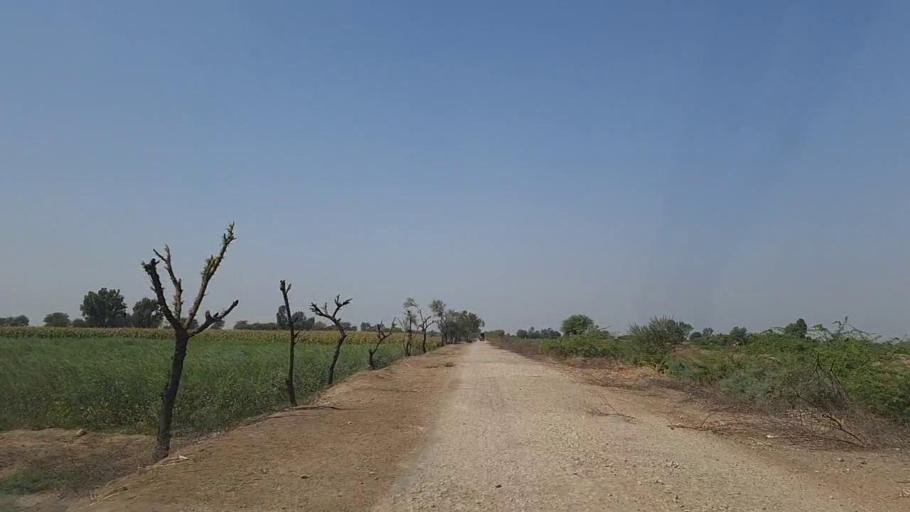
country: PK
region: Sindh
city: Samaro
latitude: 25.2243
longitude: 69.4002
